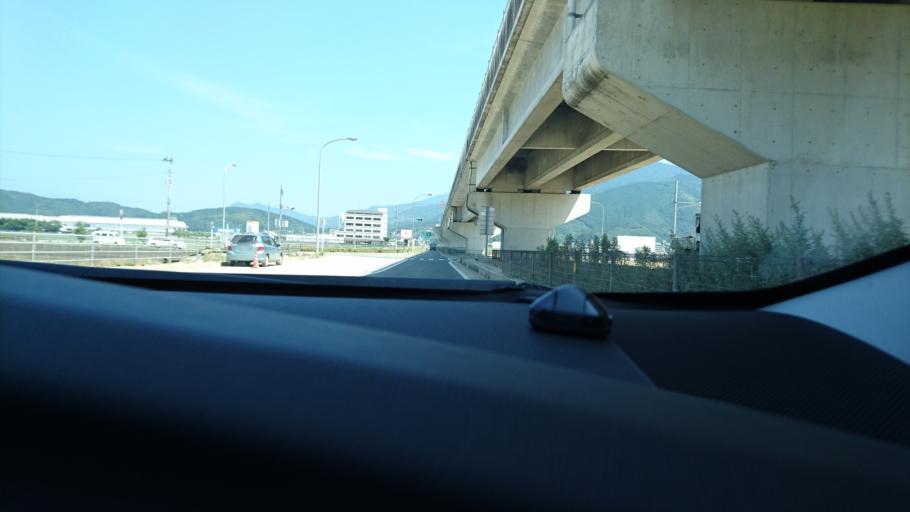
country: JP
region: Ehime
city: Ozu
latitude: 33.5236
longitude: 132.5764
